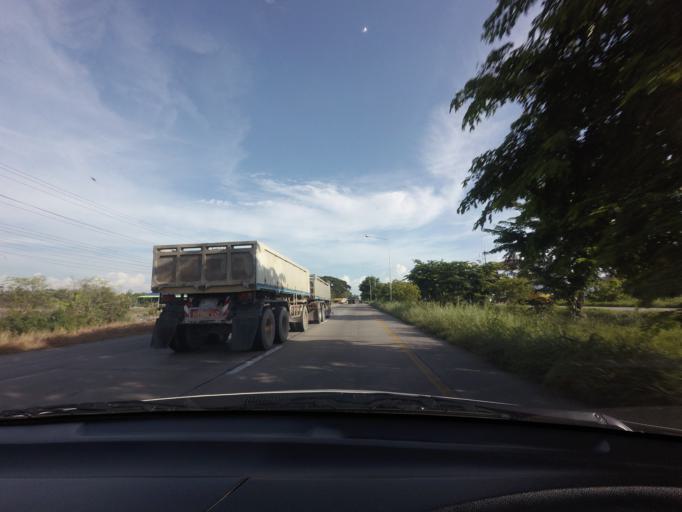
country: TH
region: Phra Nakhon Si Ayutthaya
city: Lat Bua Luang
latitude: 14.1516
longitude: 100.2907
